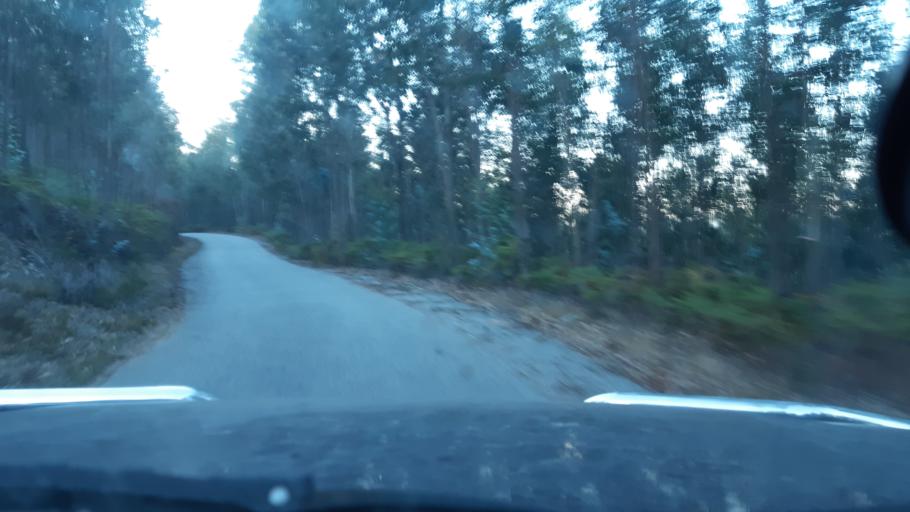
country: PT
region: Aveiro
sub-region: Agueda
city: Aguada de Cima
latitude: 40.5467
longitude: -8.2802
